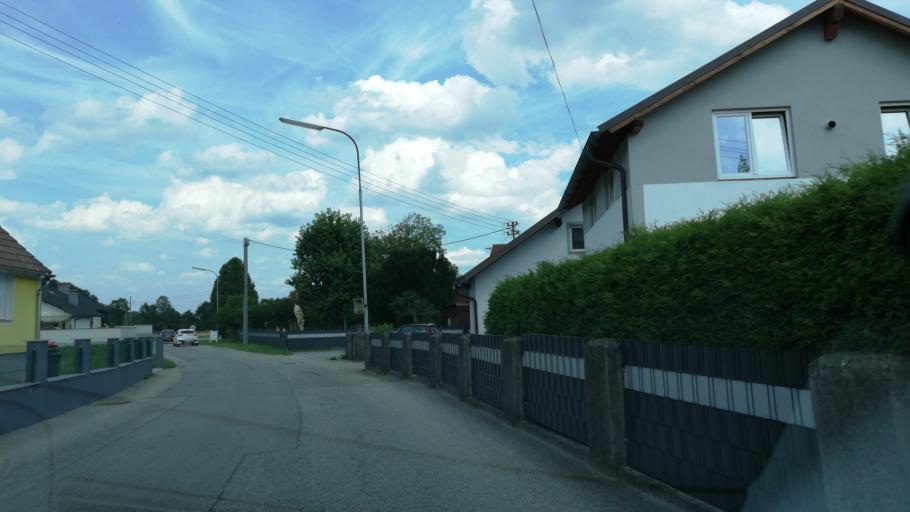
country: AT
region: Upper Austria
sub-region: Politischer Bezirk Vocklabruck
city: Attnang-Puchheim
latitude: 47.9916
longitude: 13.6944
